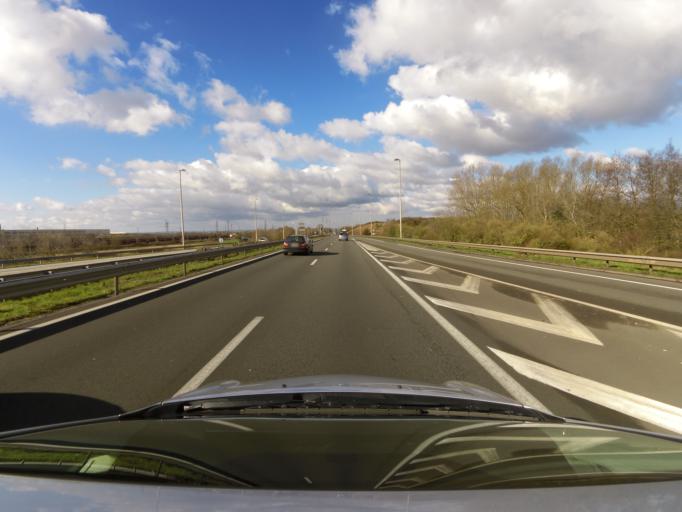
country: FR
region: Nord-Pas-de-Calais
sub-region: Departement du Nord
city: Grande-Synthe
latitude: 50.9981
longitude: 2.2872
